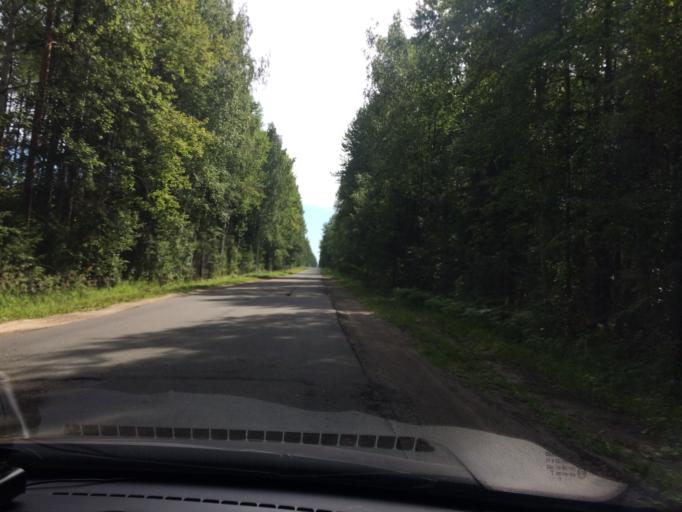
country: RU
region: Mariy-El
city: Surok
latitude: 56.5712
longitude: 48.2142
